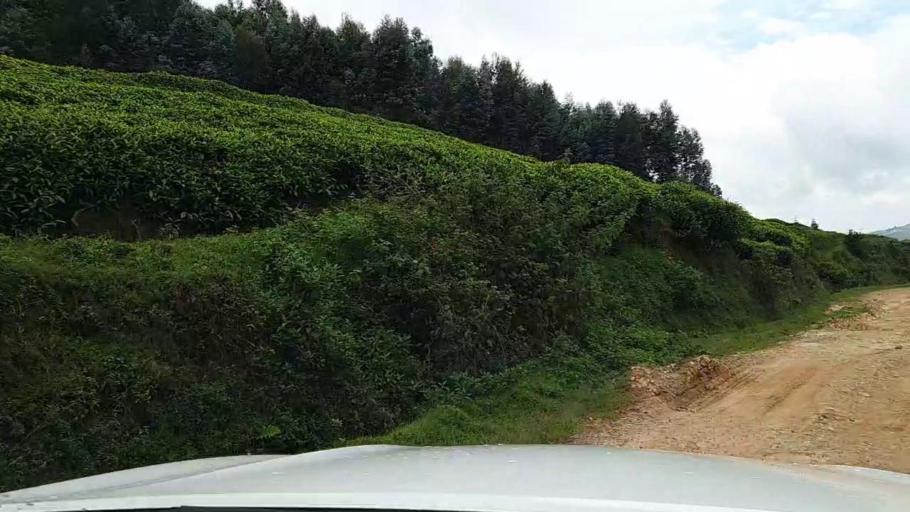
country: RW
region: Western Province
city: Kibuye
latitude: -2.2885
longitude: 29.3774
